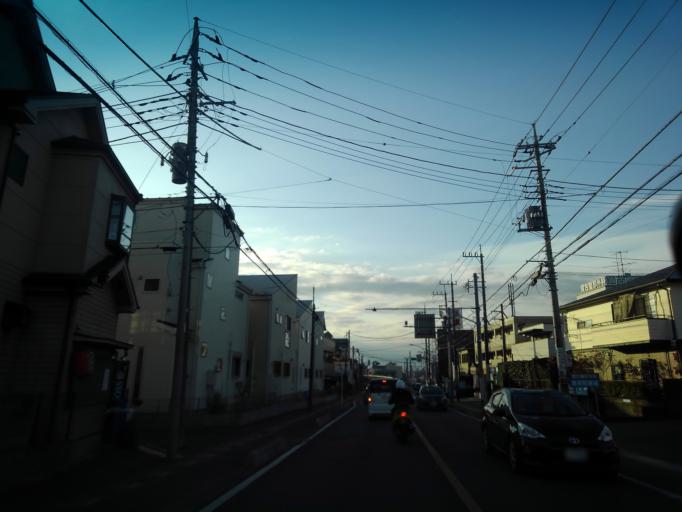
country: JP
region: Saitama
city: Tokorozawa
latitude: 35.7804
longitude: 139.4721
